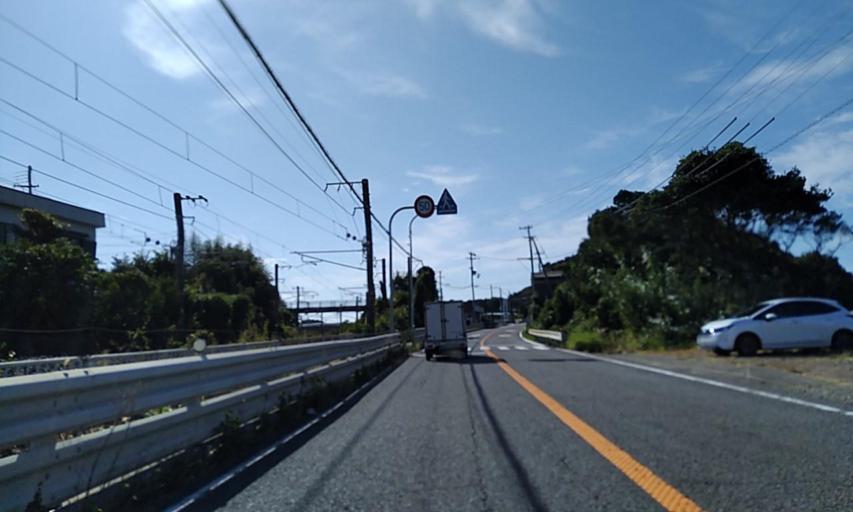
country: JP
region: Wakayama
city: Gobo
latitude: 33.7907
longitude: 135.2371
